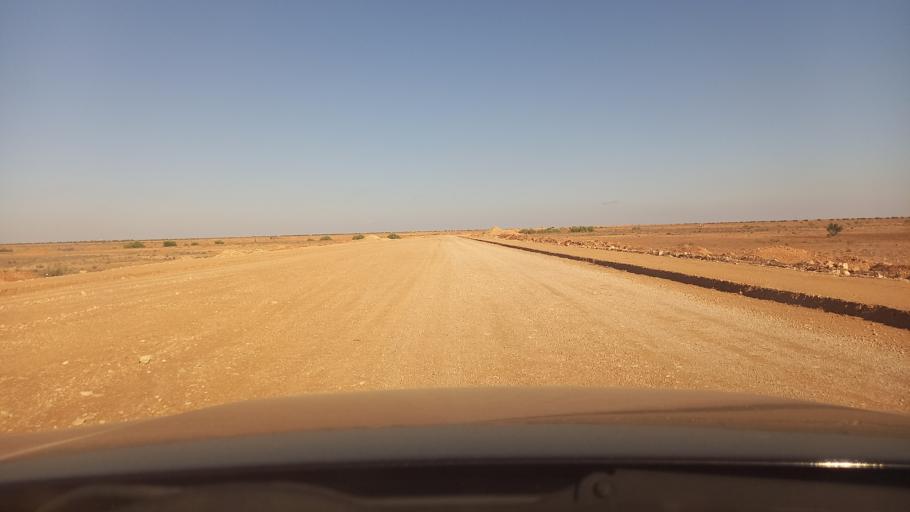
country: TN
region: Madanin
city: Medenine
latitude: 33.1415
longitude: 10.5058
